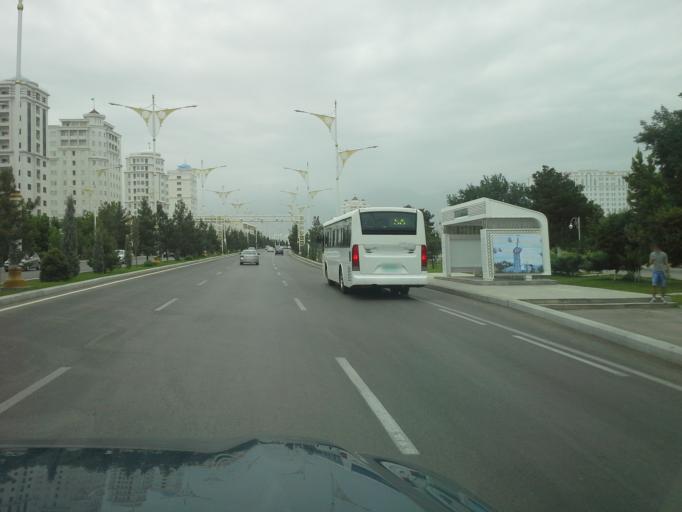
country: TM
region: Ahal
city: Ashgabat
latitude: 37.9226
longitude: 58.3752
